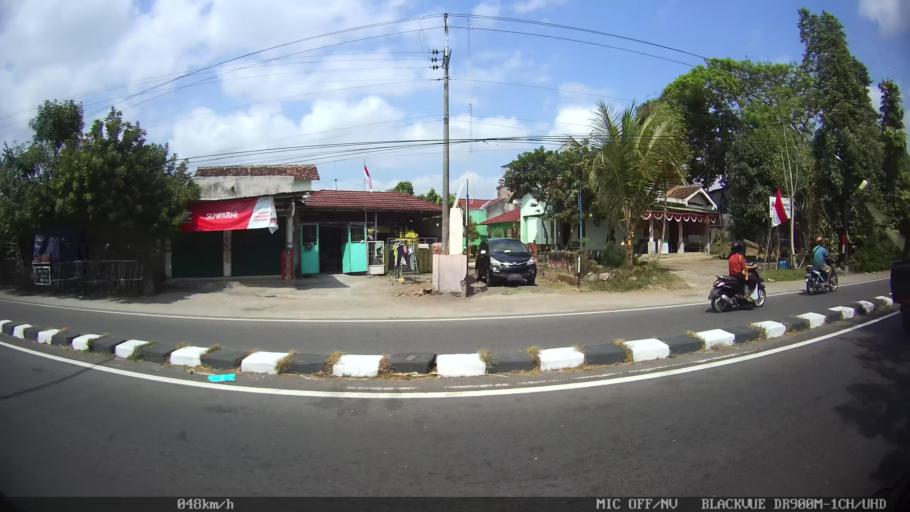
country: ID
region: Daerah Istimewa Yogyakarta
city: Kasihan
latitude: -7.8257
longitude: 110.3349
